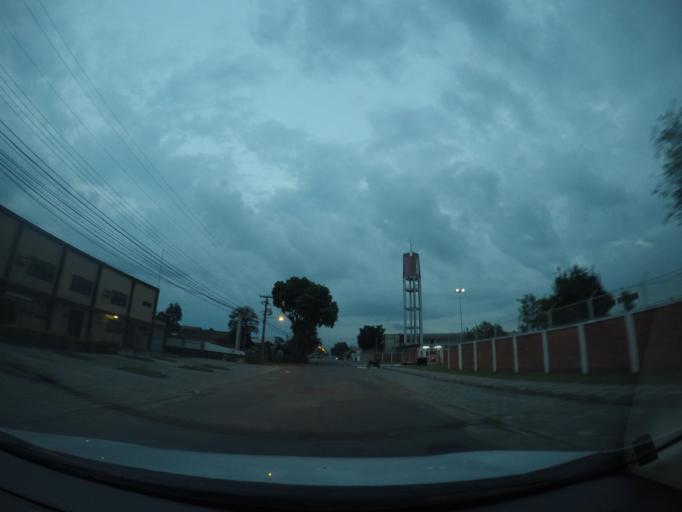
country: BR
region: Parana
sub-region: Sao Jose Dos Pinhais
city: Sao Jose dos Pinhais
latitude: -25.4944
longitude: -49.2356
